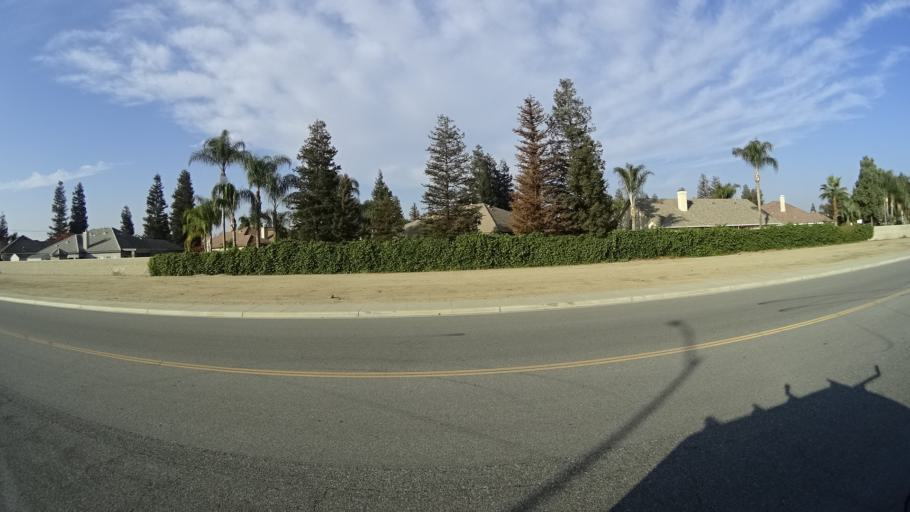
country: US
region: California
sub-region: Kern County
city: Rosedale
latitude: 35.3773
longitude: -119.1720
